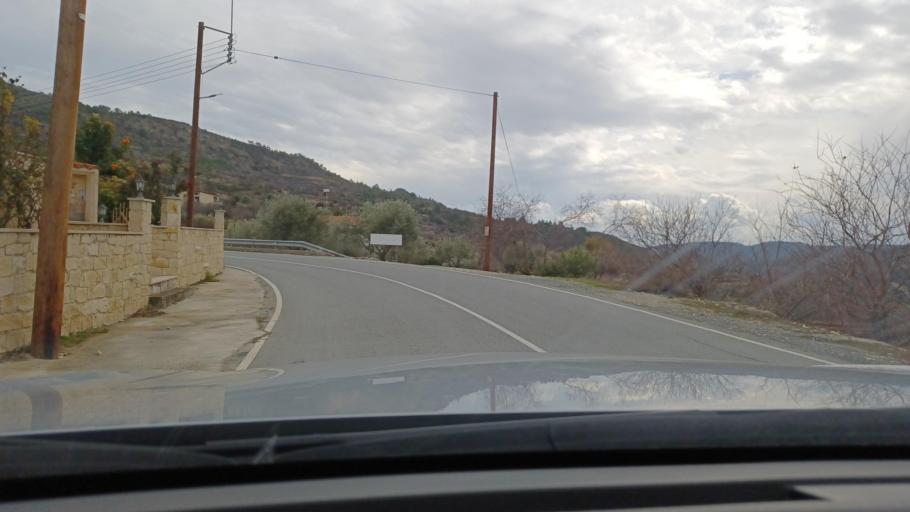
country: CY
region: Limassol
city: Pelendri
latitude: 34.8083
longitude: 32.9129
